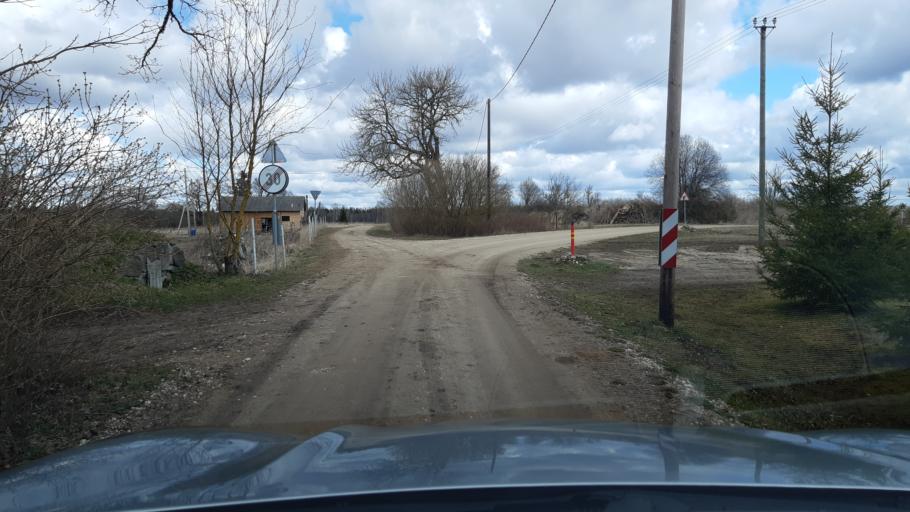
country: EE
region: Harju
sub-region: Rae vald
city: Vaida
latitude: 59.0855
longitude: 25.1365
